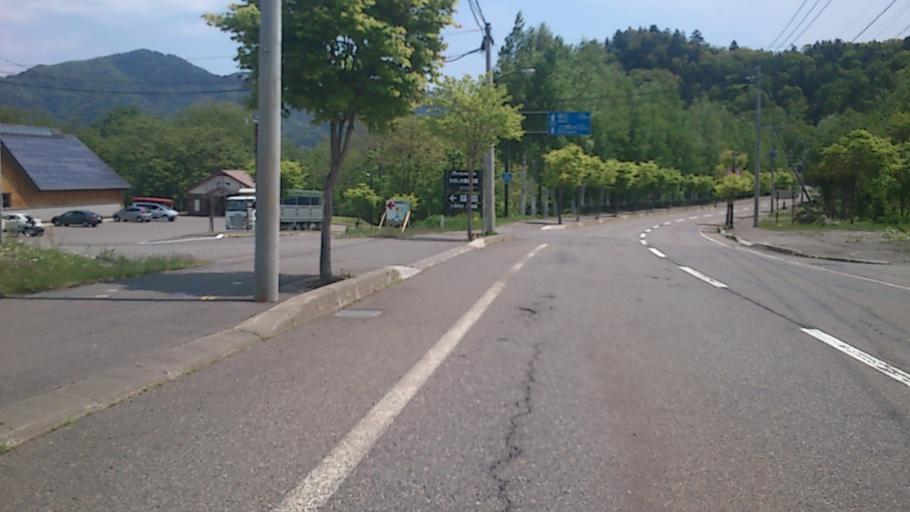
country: JP
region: Hokkaido
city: Otofuke
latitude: 43.3650
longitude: 143.1924
